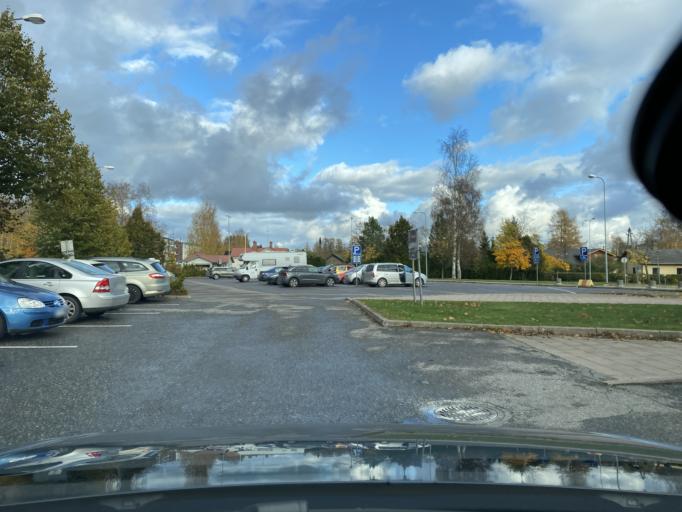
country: FI
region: Haeme
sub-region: Forssa
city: Forssa
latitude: 60.8106
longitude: 23.6180
